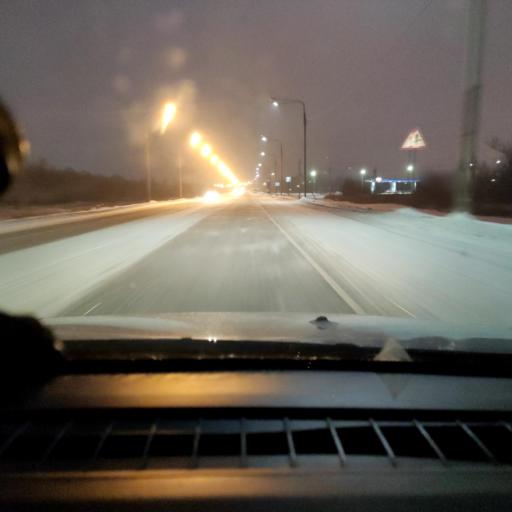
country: RU
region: Samara
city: Otradnyy
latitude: 53.3783
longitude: 51.3793
